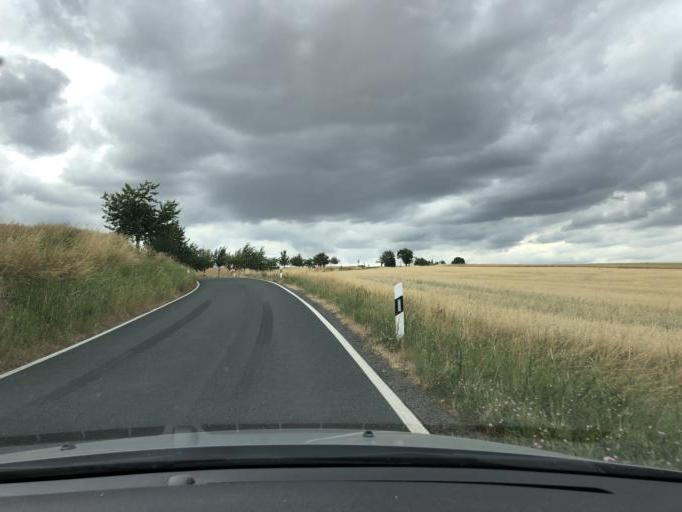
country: DE
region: Saxony
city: Geithain
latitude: 51.0185
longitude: 12.6491
